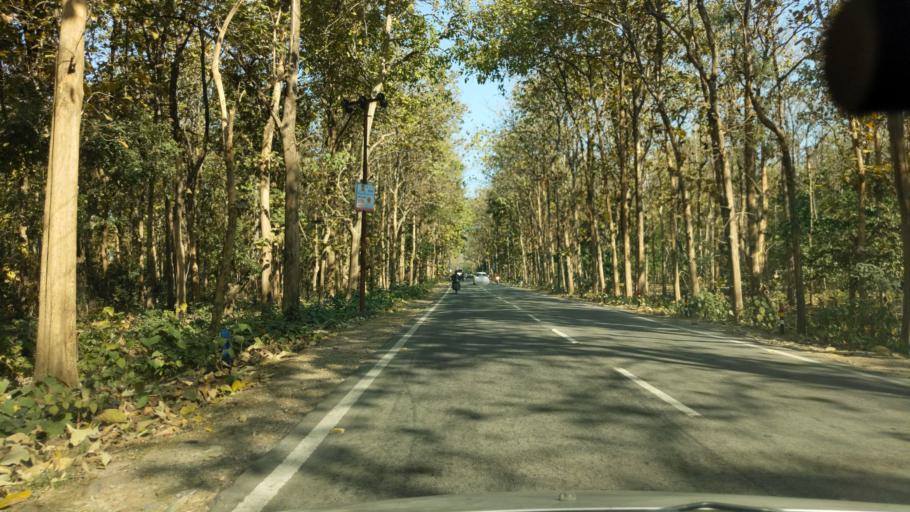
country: IN
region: Uttarakhand
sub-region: Naini Tal
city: Ramnagar
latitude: 29.3818
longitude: 79.1428
